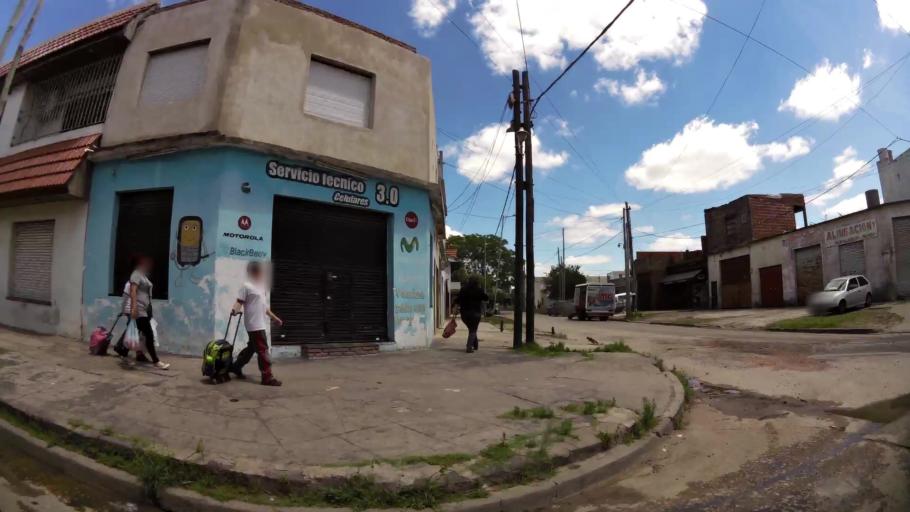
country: AR
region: Buenos Aires
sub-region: Partido de Lomas de Zamora
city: Lomas de Zamora
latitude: -34.7289
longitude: -58.4230
